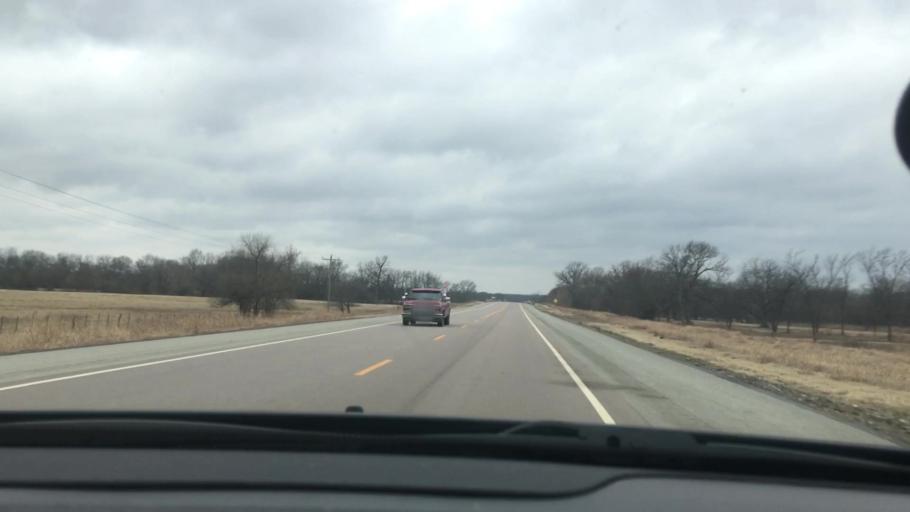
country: US
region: Oklahoma
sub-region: Atoka County
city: Atoka
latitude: 34.3730
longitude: -96.3092
